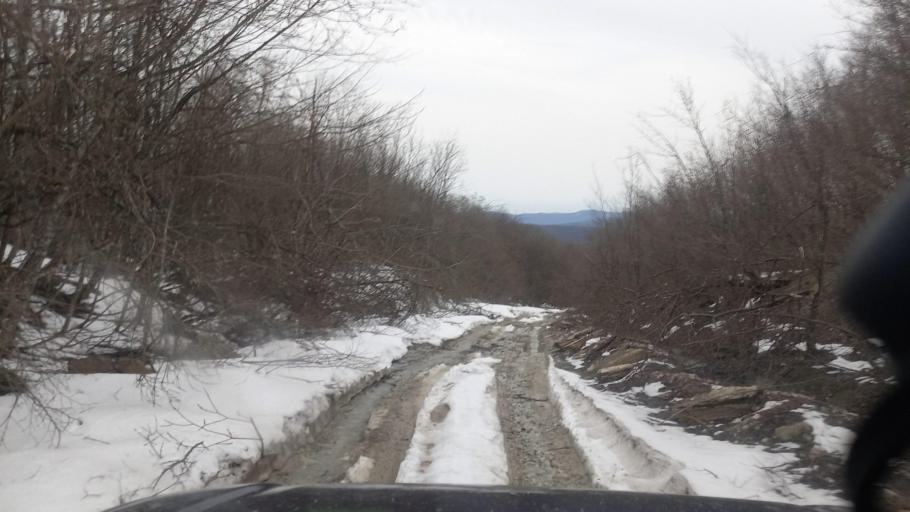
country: RU
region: Krasnodarskiy
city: Pshada
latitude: 44.5931
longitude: 38.3083
